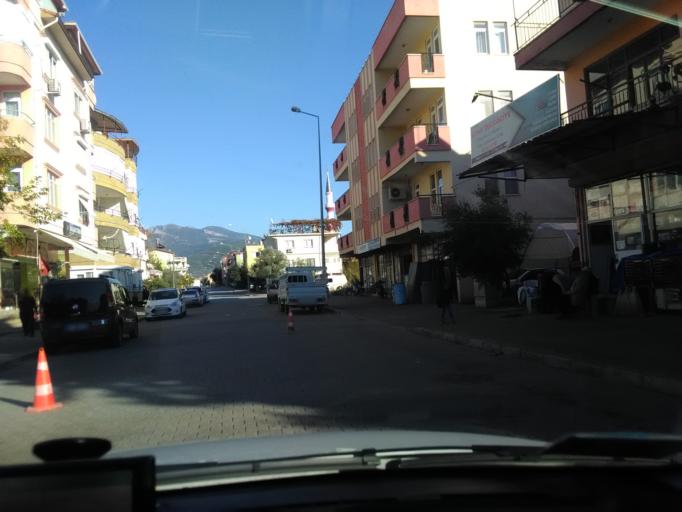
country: TR
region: Antalya
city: Gazipasa
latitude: 36.2692
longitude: 32.3226
